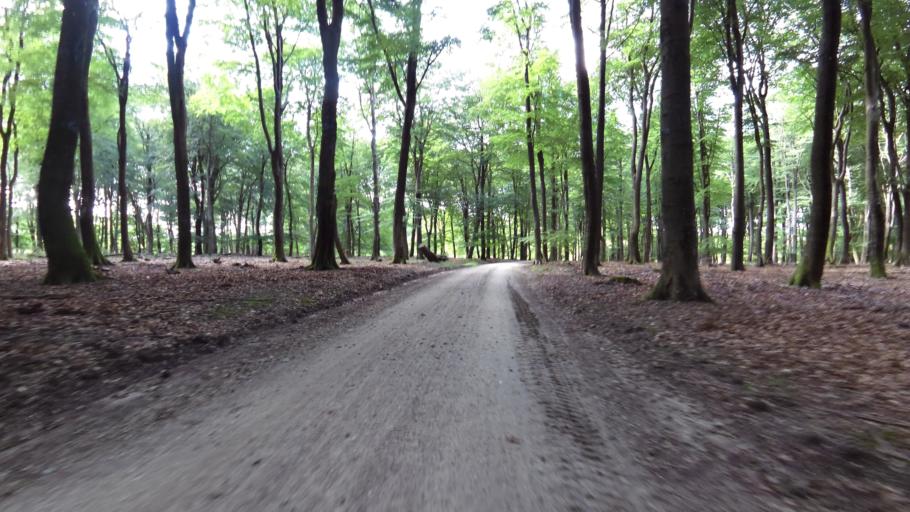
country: NL
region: Gelderland
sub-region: Gemeente Apeldoorn
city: Uddel
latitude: 52.2958
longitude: 5.8638
